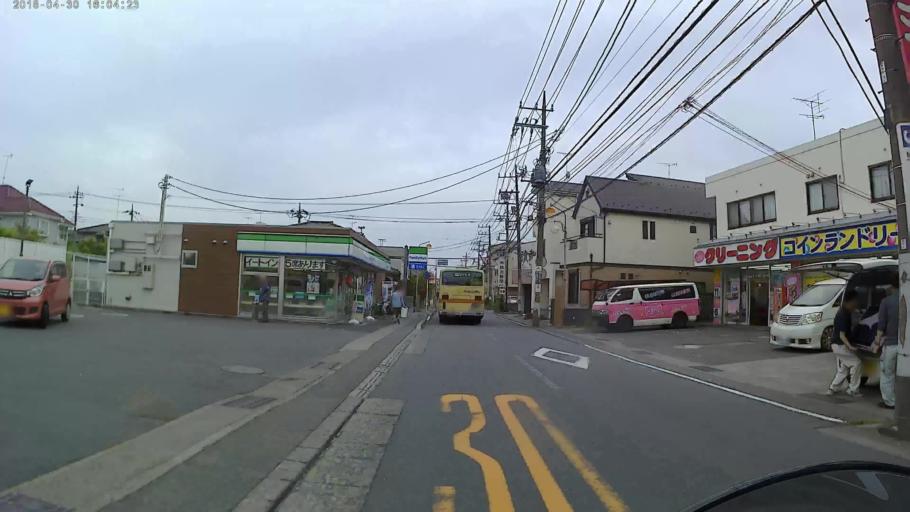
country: JP
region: Kanagawa
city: Minami-rinkan
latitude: 35.5097
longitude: 139.4239
